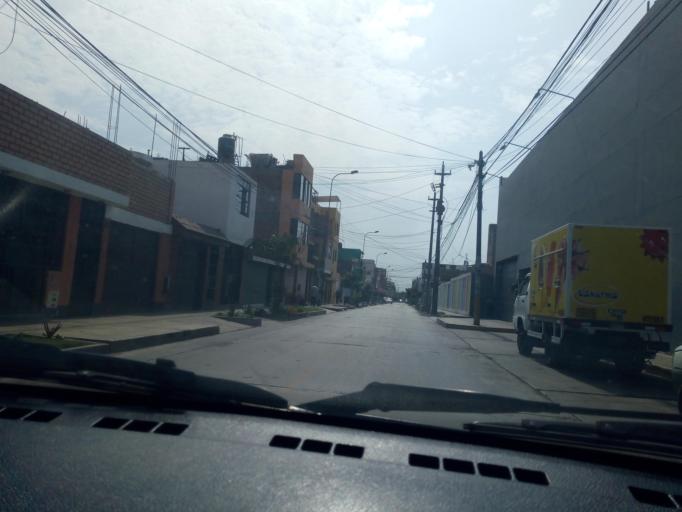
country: PE
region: Lima
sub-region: Lima
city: Independencia
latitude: -11.9950
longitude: -77.0722
